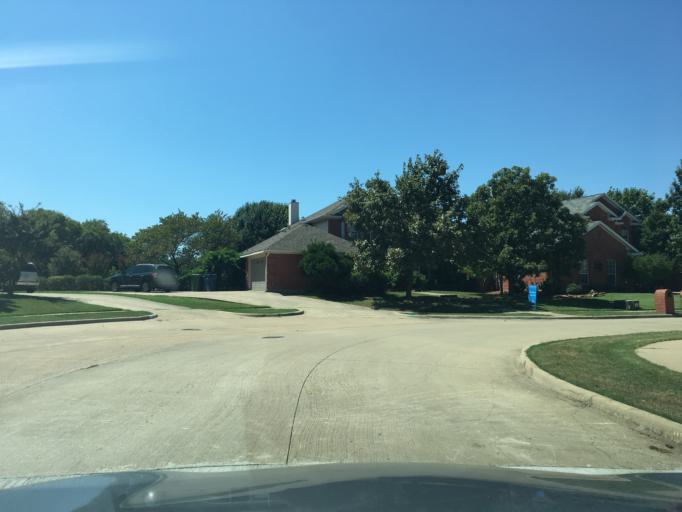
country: US
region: Texas
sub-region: Dallas County
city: Sachse
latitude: 32.9635
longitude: -96.6309
